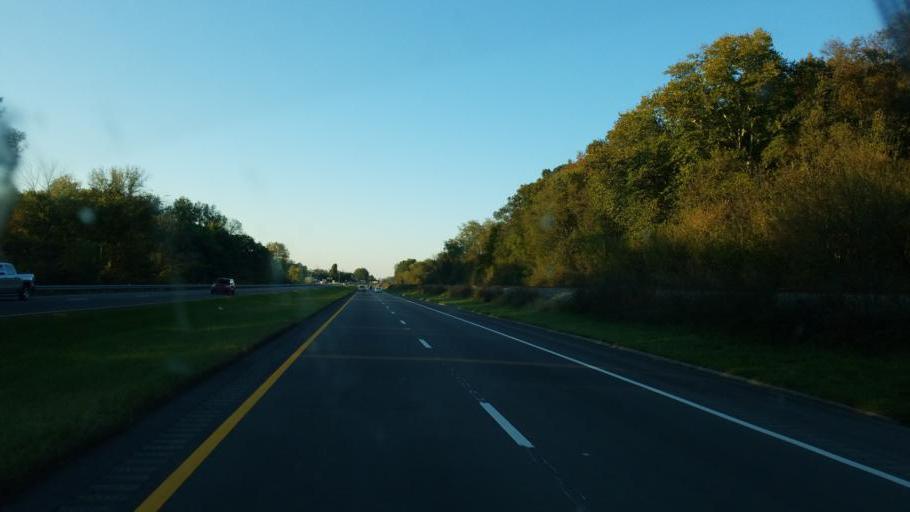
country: US
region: Ohio
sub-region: Scioto County
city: Lucasville
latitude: 38.8663
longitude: -82.9922
